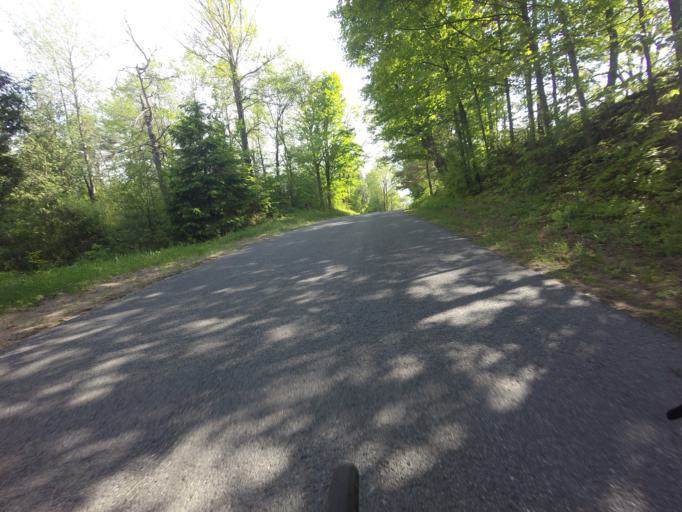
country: US
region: New York
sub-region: St. Lawrence County
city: Gouverneur
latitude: 44.2304
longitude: -75.2270
